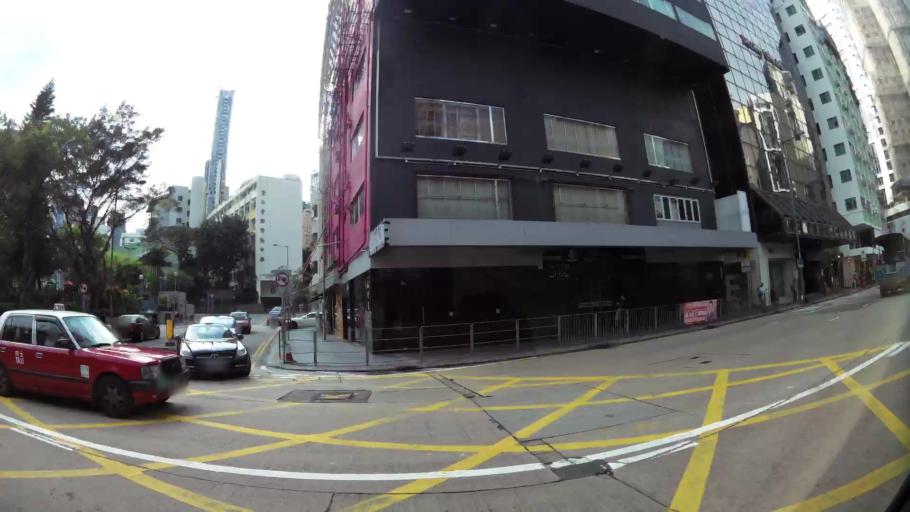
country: HK
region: Wanchai
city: Wan Chai
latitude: 22.2757
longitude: 114.1801
